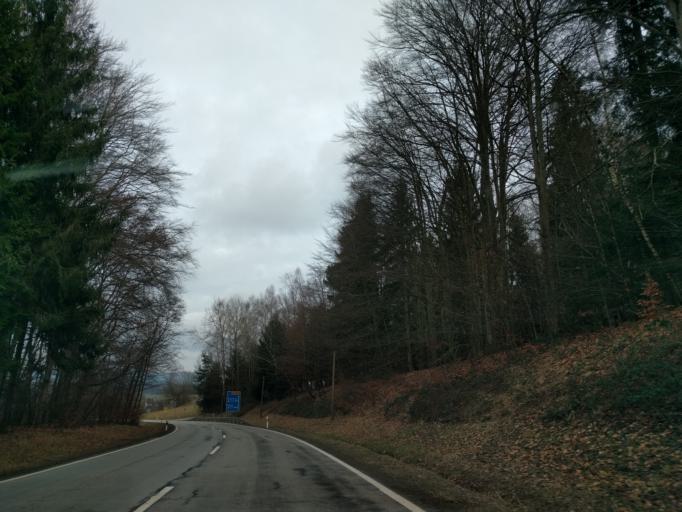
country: DE
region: Bavaria
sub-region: Lower Bavaria
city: Iggensbach
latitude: 48.7249
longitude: 13.1330
